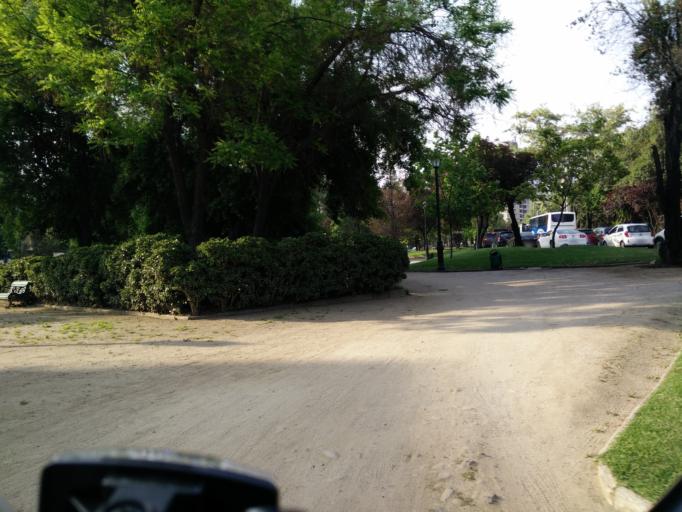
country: CL
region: Santiago Metropolitan
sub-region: Provincia de Santiago
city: Villa Presidente Frei, Nunoa, Santiago, Chile
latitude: -33.4089
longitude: -70.5872
